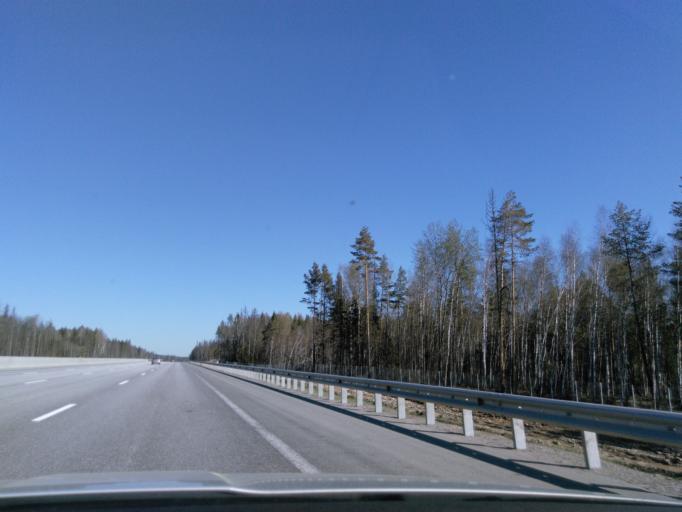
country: RU
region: Moskovskaya
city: Rzhavki
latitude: 56.0105
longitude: 37.2865
